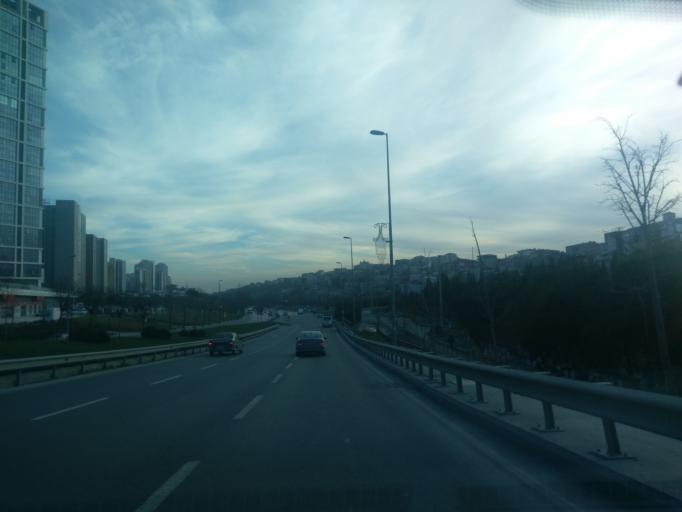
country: TR
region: Istanbul
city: Basaksehir
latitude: 41.0584
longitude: 28.7581
